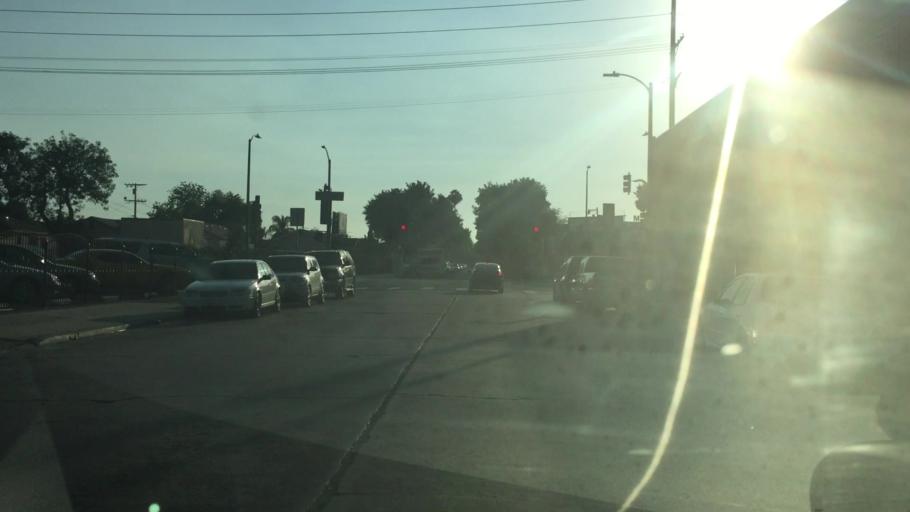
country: US
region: California
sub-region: Los Angeles County
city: Florence-Graham
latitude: 33.9638
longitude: -118.2689
